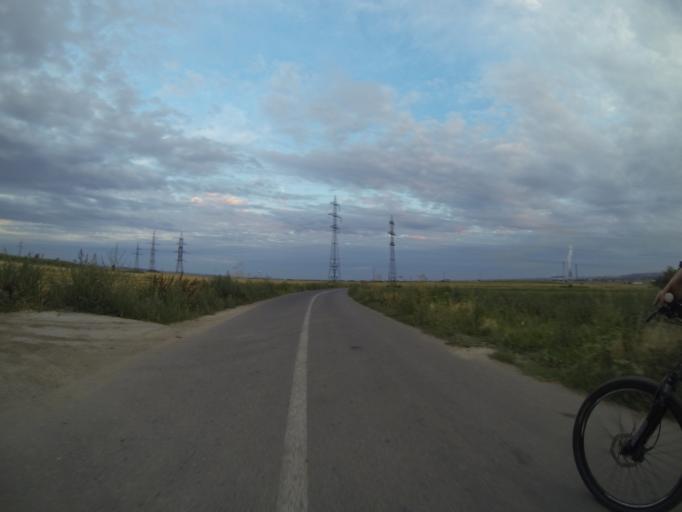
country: RO
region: Dolj
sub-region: Comuna Isalnita
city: Isalnita
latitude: 44.4153
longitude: 23.7295
